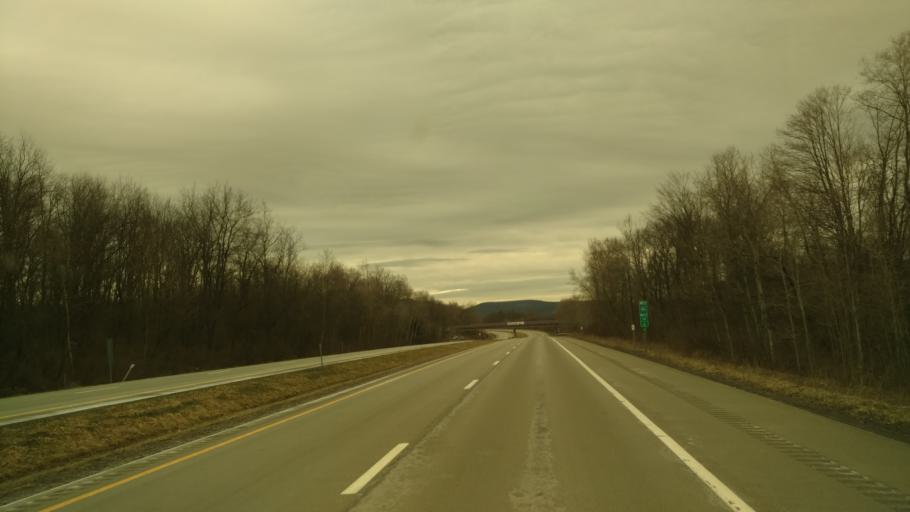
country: US
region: New York
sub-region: Cattaraugus County
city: Salamanca
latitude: 42.1395
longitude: -78.7744
